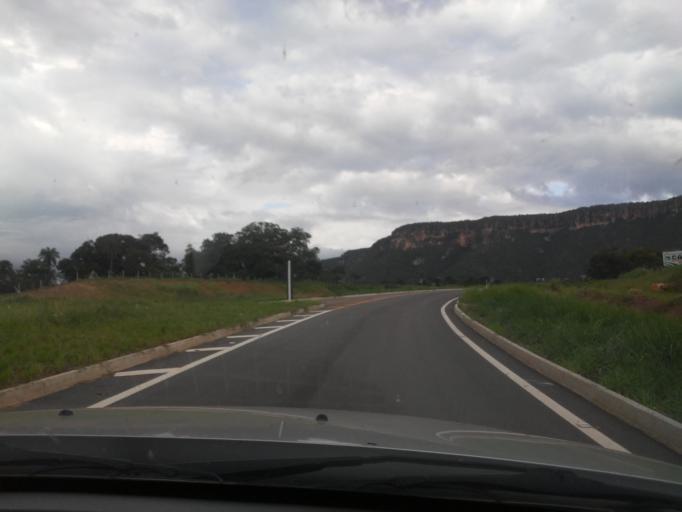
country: BR
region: Tocantins
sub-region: Taguatinga
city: Taguatinga
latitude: -12.3881
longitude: -46.4135
